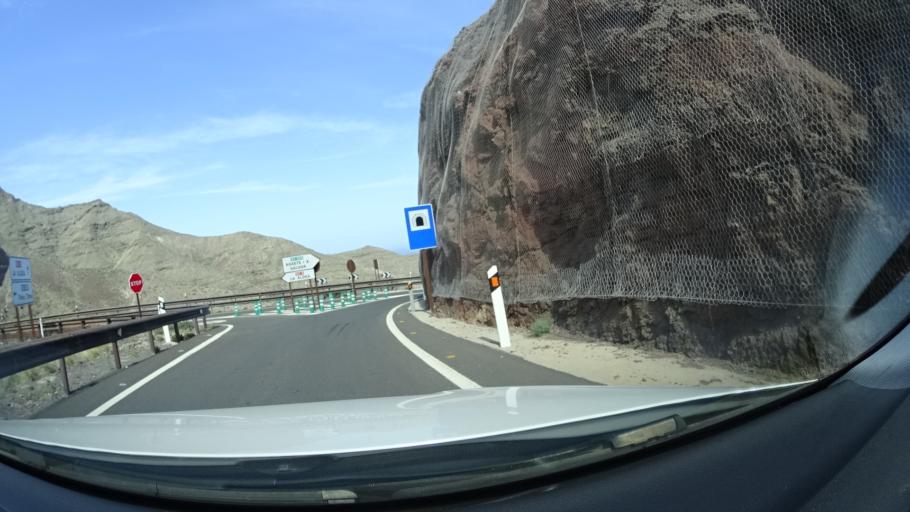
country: ES
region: Canary Islands
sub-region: Provincia de Las Palmas
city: San Nicolas
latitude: 28.0403
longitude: -15.7354
